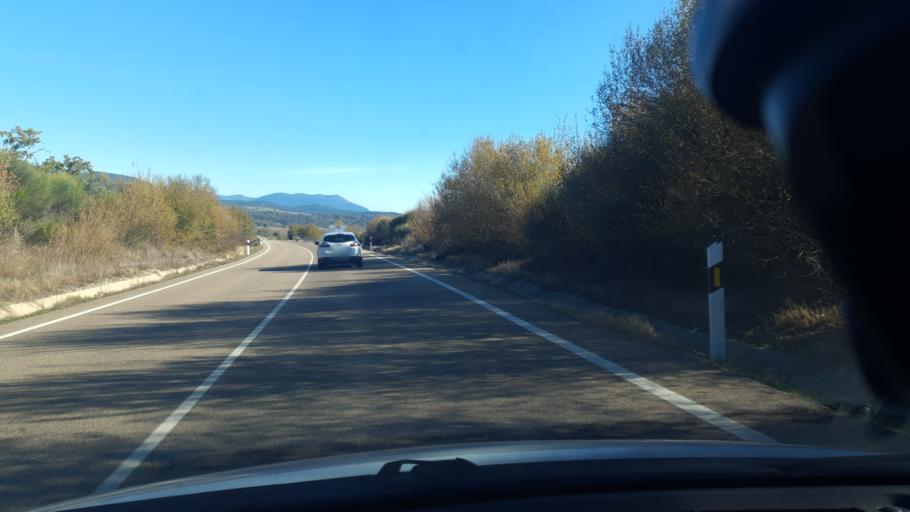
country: ES
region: Castille and Leon
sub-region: Provincia de Avila
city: Candeleda
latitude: 40.1350
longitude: -5.2239
